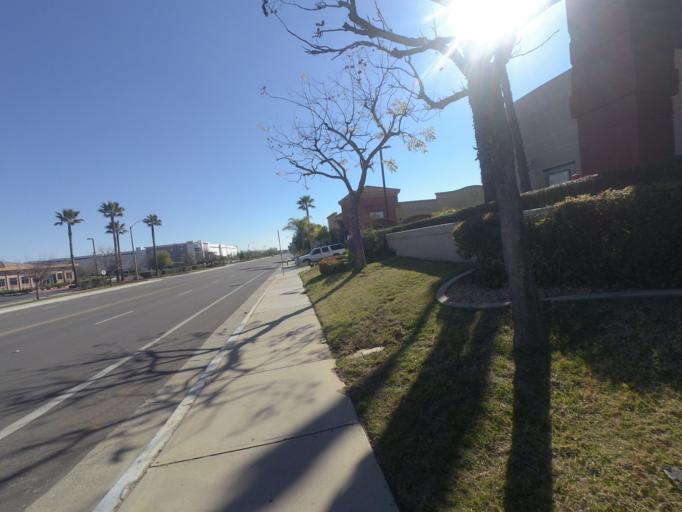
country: US
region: California
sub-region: Riverside County
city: March Air Force Base
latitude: 33.9166
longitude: -117.2701
